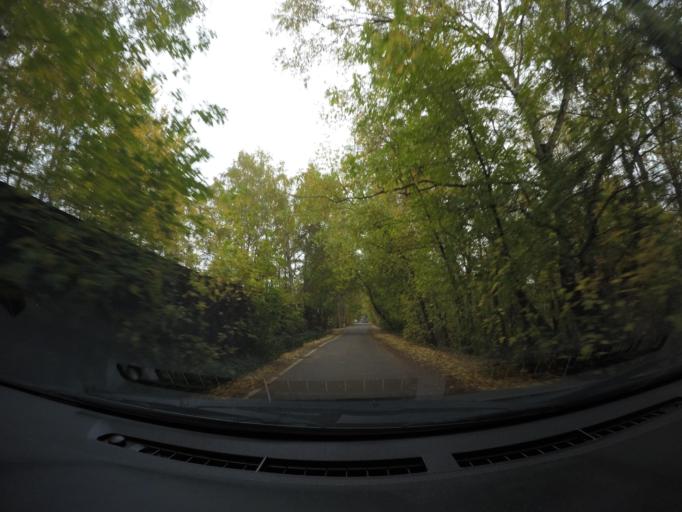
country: RU
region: Moskovskaya
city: Imeni Vorovskogo
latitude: 55.7304
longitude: 38.3172
